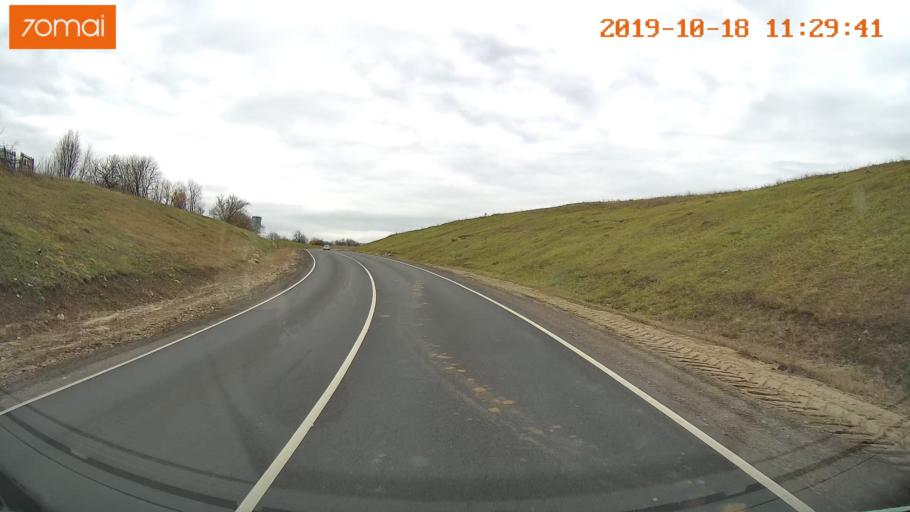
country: RU
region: Rjazan
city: Oktyabr'skiy
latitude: 54.1557
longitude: 38.6803
